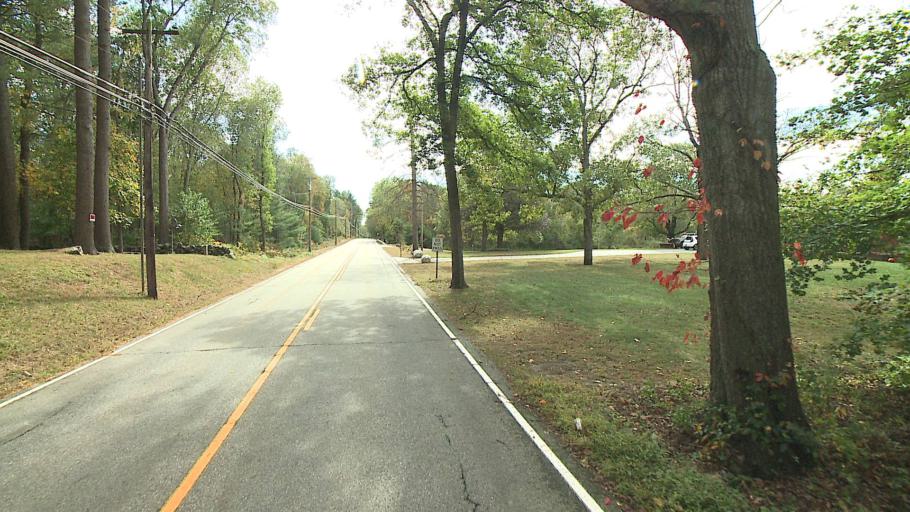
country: US
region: Connecticut
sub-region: Windham County
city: Killingly Center
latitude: 41.8813
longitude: -71.8750
